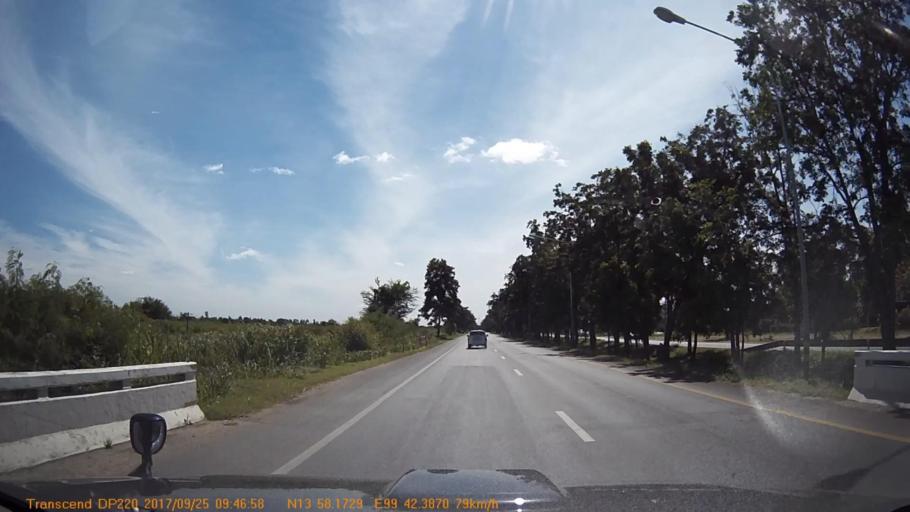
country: TH
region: Kanchanaburi
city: Tha Muang
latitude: 13.9695
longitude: 99.7069
